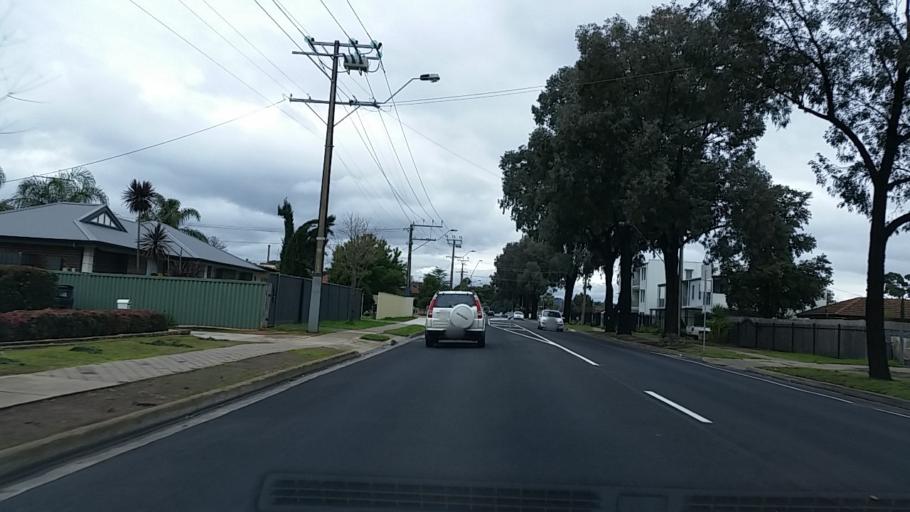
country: AU
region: South Australia
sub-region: Salisbury
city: Salisbury
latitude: -34.7688
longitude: 138.6307
